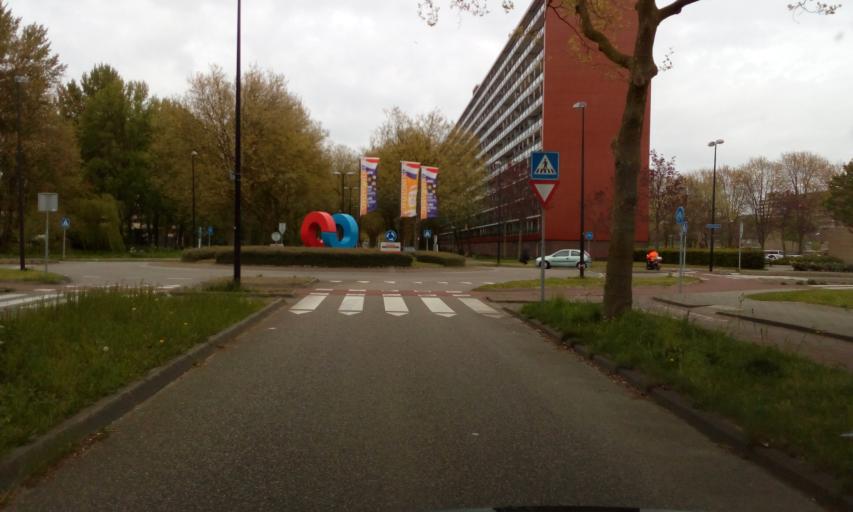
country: NL
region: South Holland
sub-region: Gemeente Vlaardingen
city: Vlaardingen
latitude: 51.9296
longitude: 4.3515
